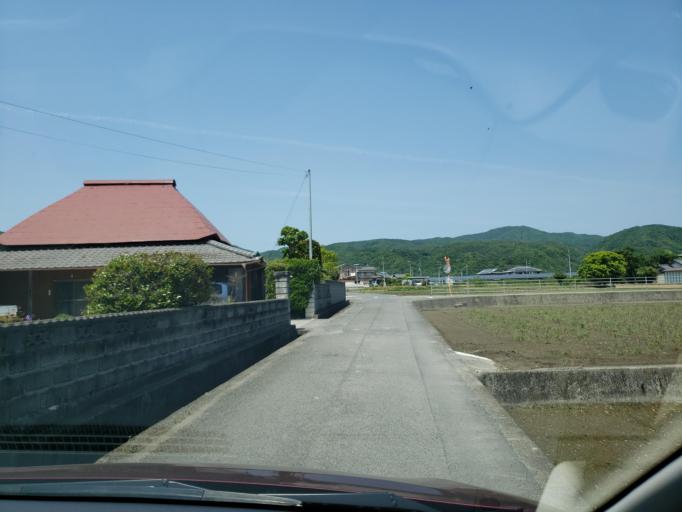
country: JP
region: Tokushima
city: Kamojimacho-jogejima
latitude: 34.0966
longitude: 134.2685
